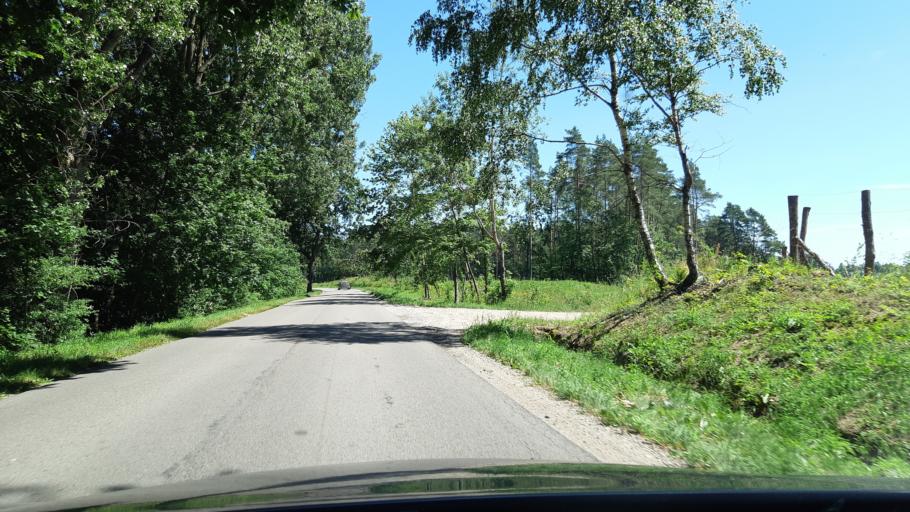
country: PL
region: Warmian-Masurian Voivodeship
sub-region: Powiat gizycki
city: Gizycko
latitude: 53.9726
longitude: 21.8202
